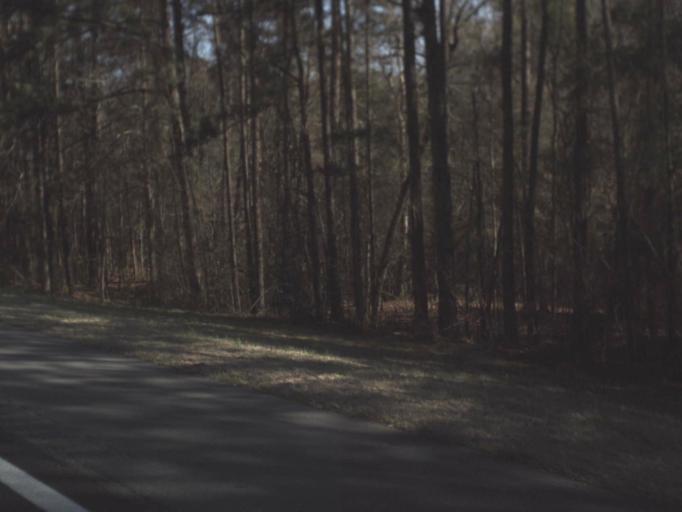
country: US
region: Florida
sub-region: Gadsden County
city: Chattahoochee
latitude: 30.6220
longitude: -84.7869
